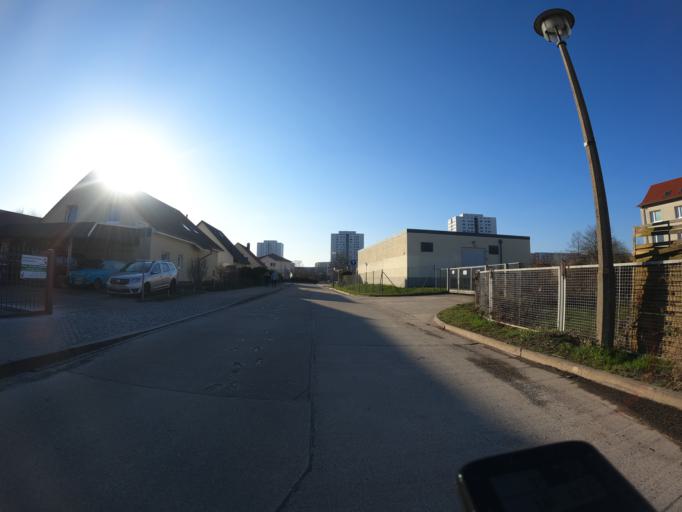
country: DE
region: Berlin
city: Marzahn
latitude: 52.5434
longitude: 13.5562
